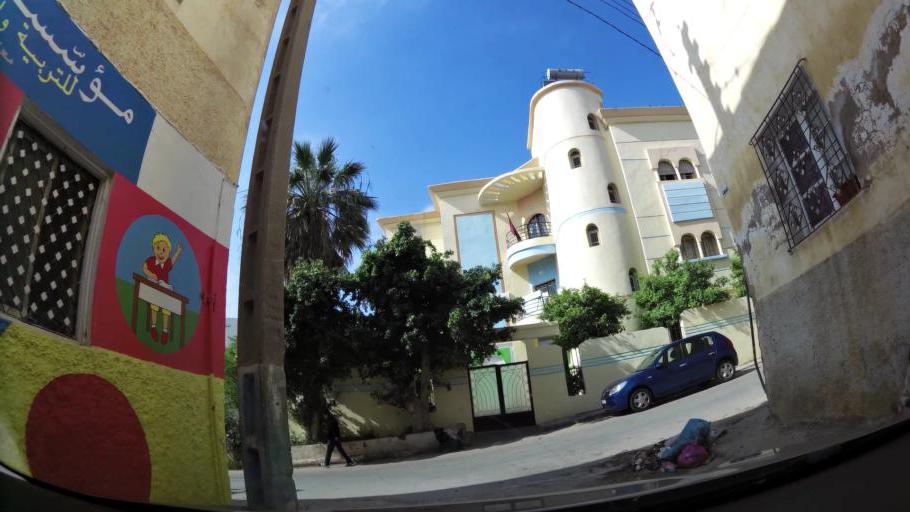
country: MA
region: Fes-Boulemane
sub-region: Fes
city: Fes
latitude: 34.0654
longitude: -5.0087
